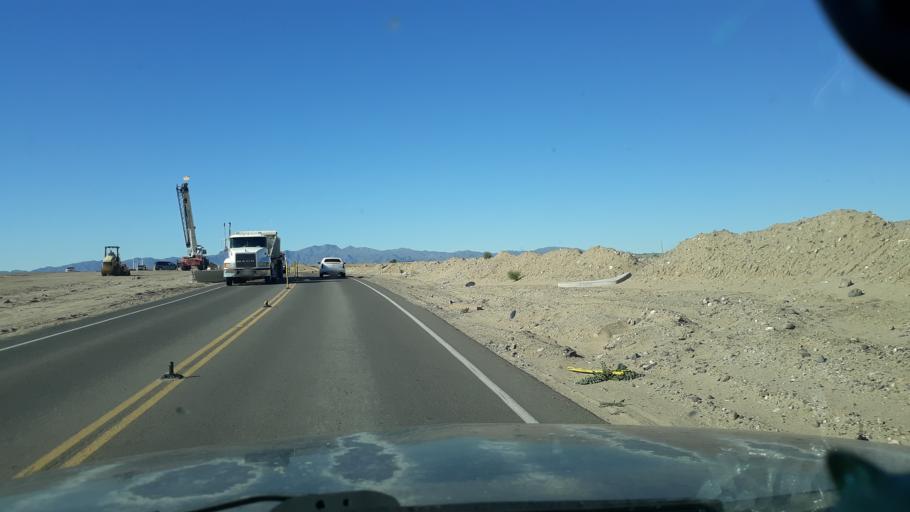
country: US
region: Arizona
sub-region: Maricopa County
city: Youngtown
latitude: 33.5512
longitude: -112.3134
